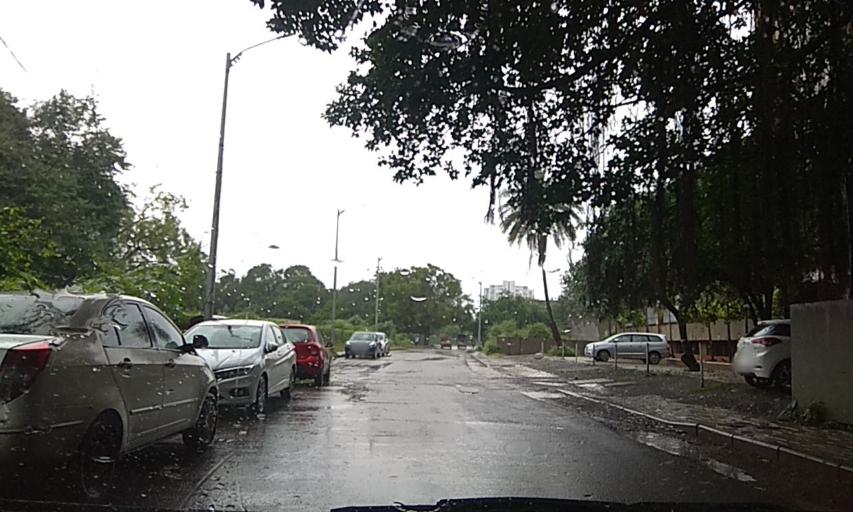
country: IN
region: Maharashtra
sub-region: Pune Division
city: Khadki
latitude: 18.5565
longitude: 73.7992
